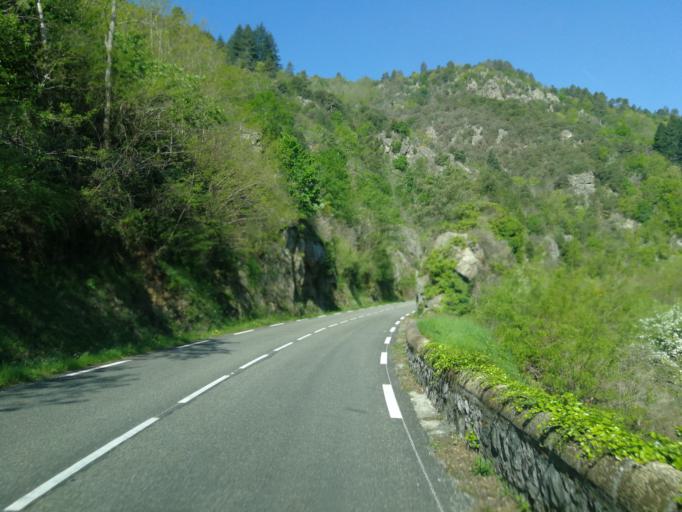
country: FR
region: Rhone-Alpes
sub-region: Departement de l'Ardeche
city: Saint-Sauveur-de-Montagut
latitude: 44.8371
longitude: 4.5754
